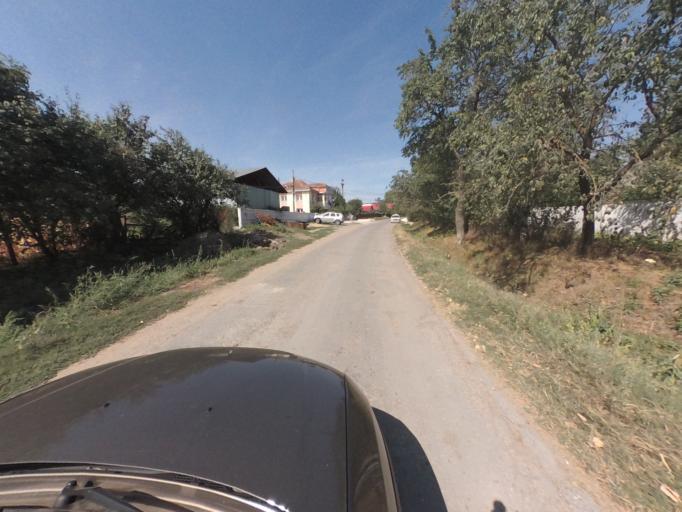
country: RO
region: Vaslui
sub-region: Comuna Deleni
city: Deleni
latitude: 46.5411
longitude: 27.7469
